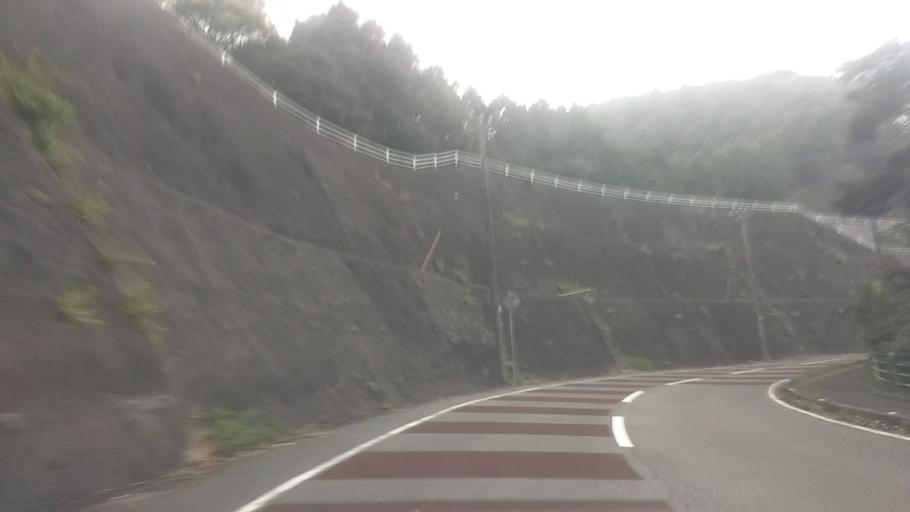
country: JP
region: Chiba
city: Kawaguchi
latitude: 35.1490
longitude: 140.1493
